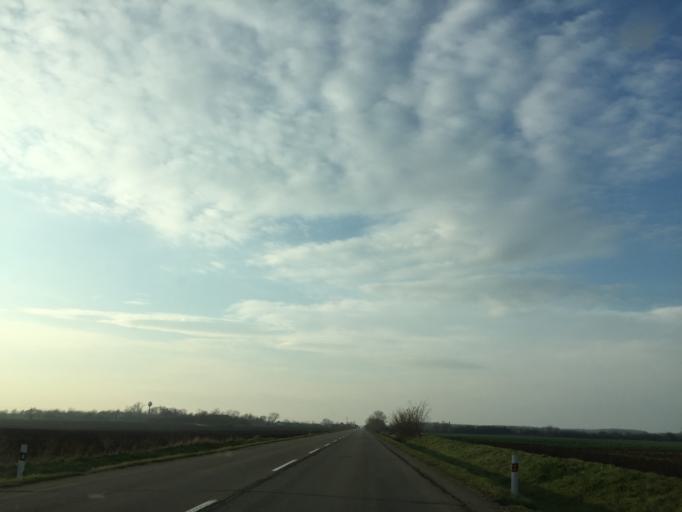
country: SK
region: Nitriansky
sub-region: Okres Komarno
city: Hurbanovo
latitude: 47.9168
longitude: 18.2710
